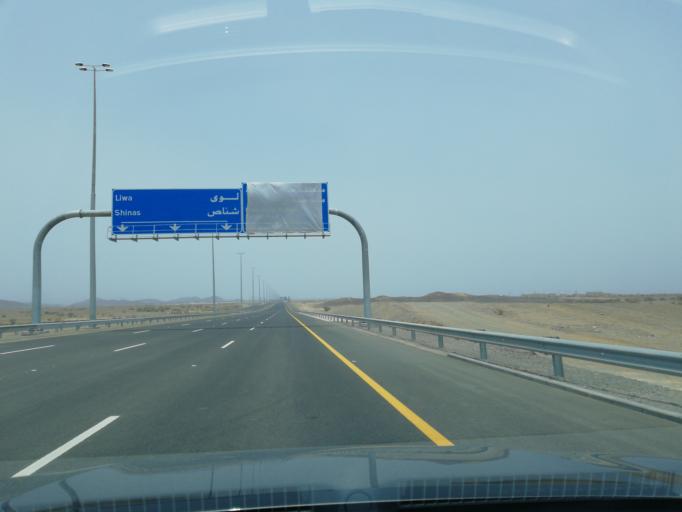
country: OM
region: Al Batinah
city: Al Liwa'
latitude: 24.4340
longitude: 56.5252
